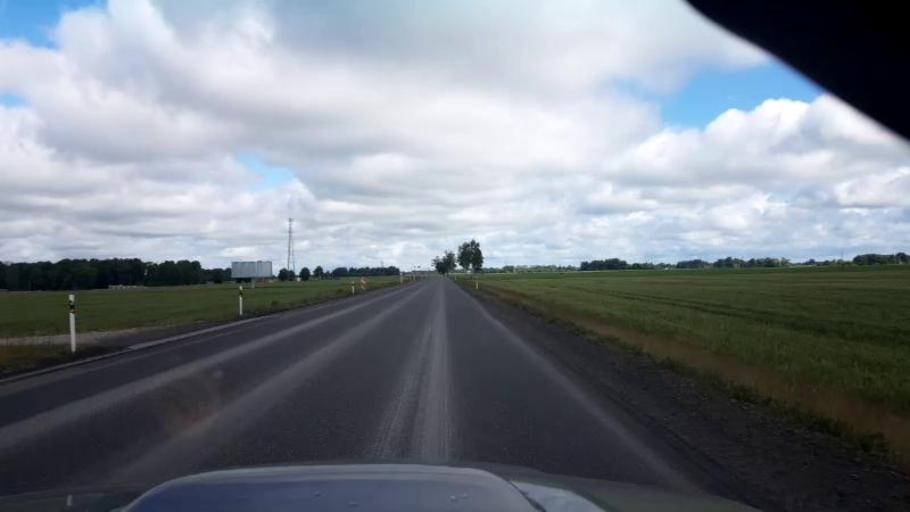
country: LV
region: Bauskas Rajons
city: Bauska
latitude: 56.2872
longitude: 24.3571
